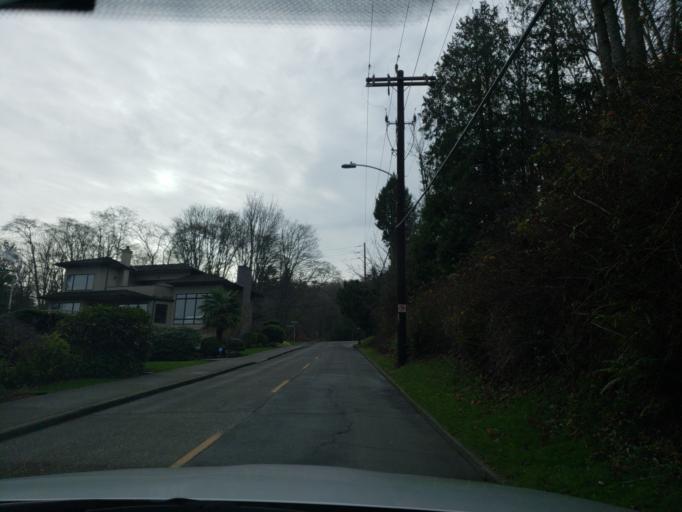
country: US
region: Washington
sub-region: King County
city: Seattle
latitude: 47.6657
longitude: -122.4093
